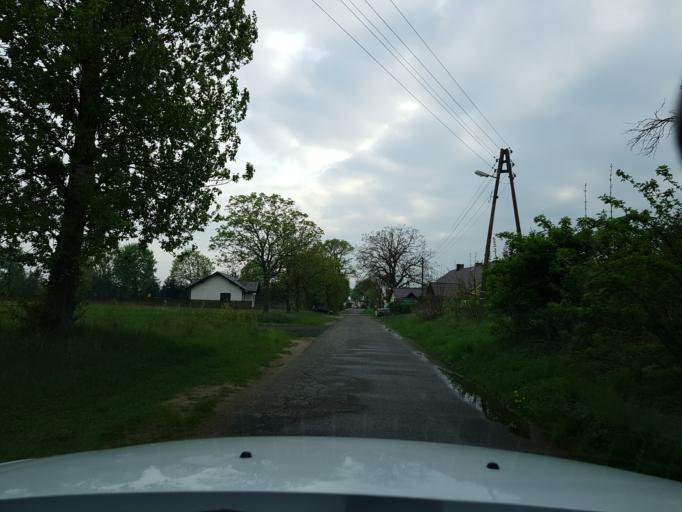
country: PL
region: West Pomeranian Voivodeship
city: Trzcinsko Zdroj
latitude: 52.9781
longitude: 14.6721
